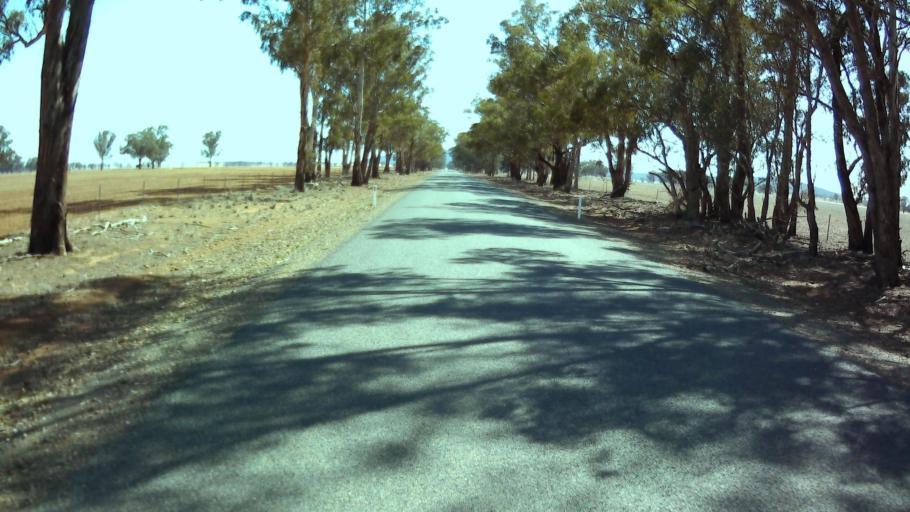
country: AU
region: New South Wales
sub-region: Weddin
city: Grenfell
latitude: -33.7194
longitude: 147.9014
